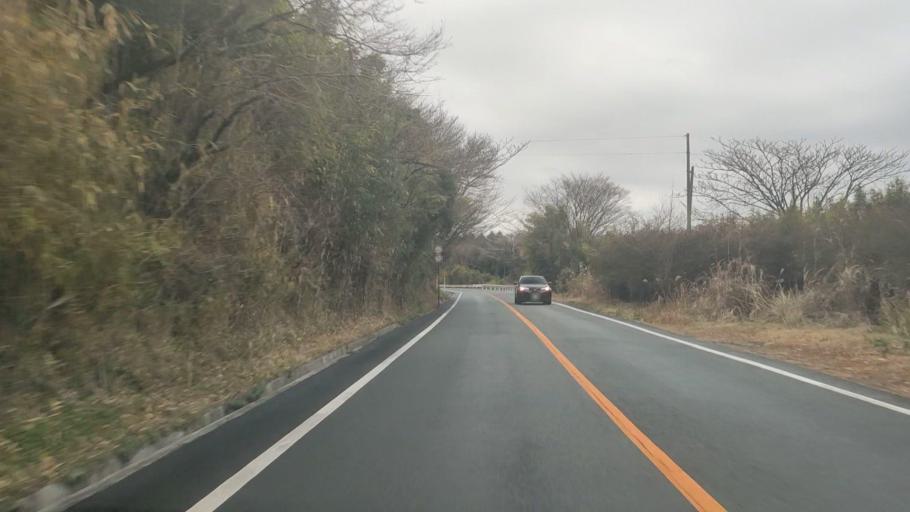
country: JP
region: Kumamoto
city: Aso
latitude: 32.8969
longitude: 131.0180
